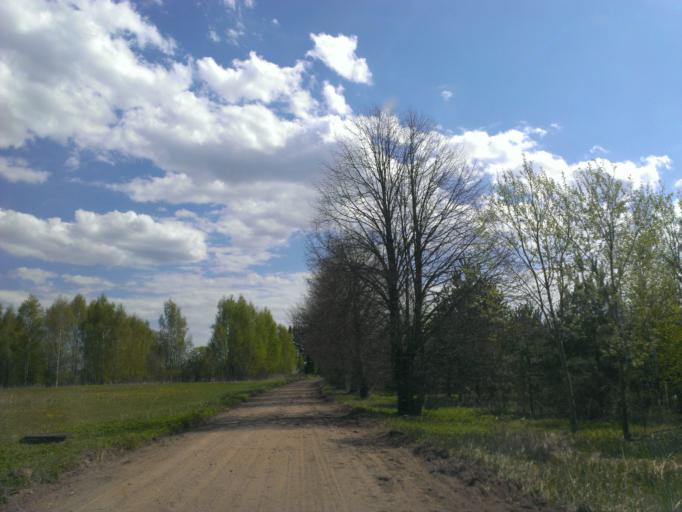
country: LV
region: Saulkrastu
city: Saulkrasti
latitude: 57.3614
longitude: 24.4910
